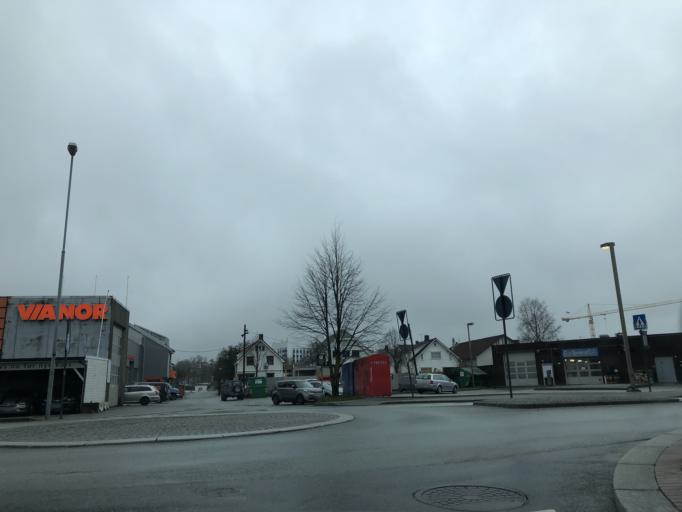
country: NO
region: Rogaland
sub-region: Sandnes
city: Sandnes
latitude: 58.8491
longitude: 5.7380
